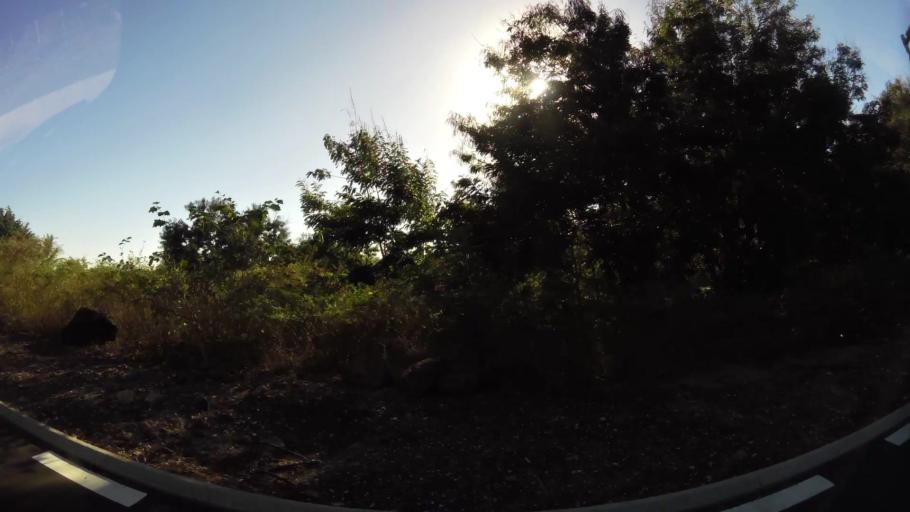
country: MU
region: Black River
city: Tamarin
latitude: -20.3429
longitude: 57.3904
